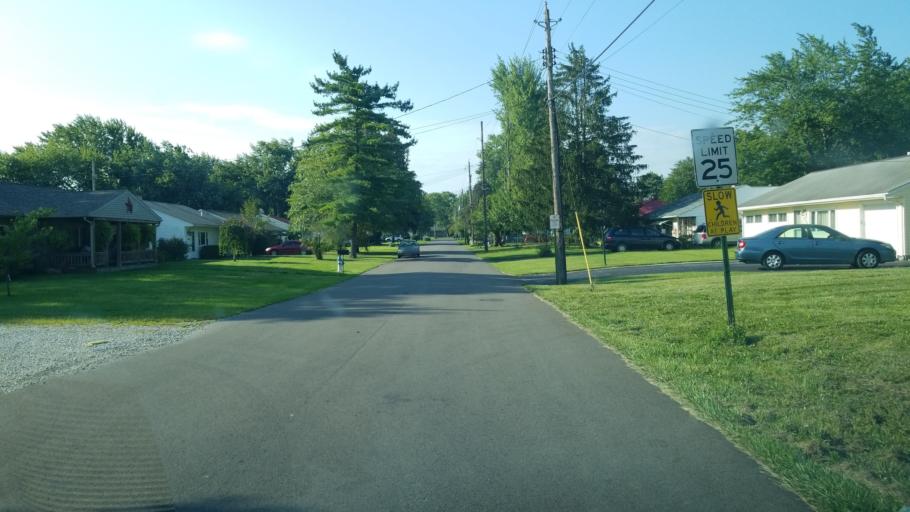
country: US
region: Ohio
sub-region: Marion County
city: Marion
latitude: 40.5880
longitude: -83.0963
